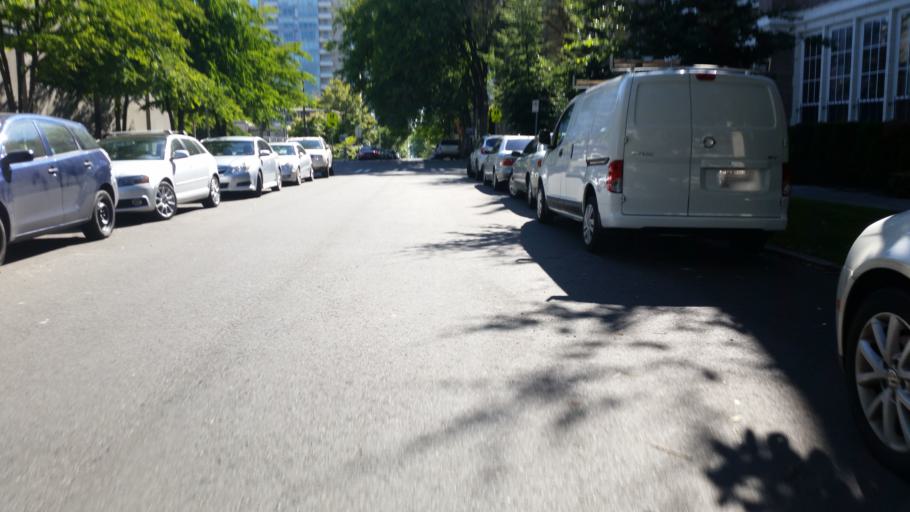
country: US
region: Washington
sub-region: King County
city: Seattle
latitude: 47.6077
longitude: -122.3244
